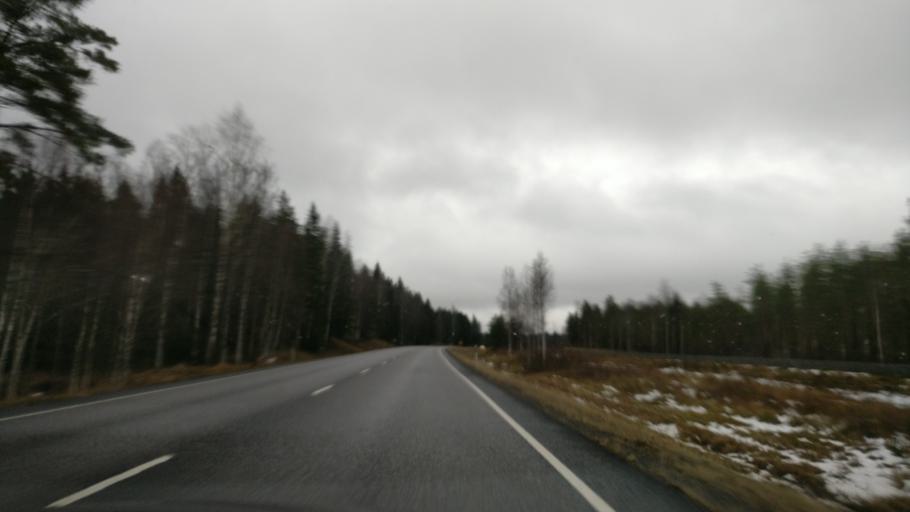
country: FI
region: Uusimaa
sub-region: Raaseporin
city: Ekenaes
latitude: 59.9408
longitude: 23.3398
